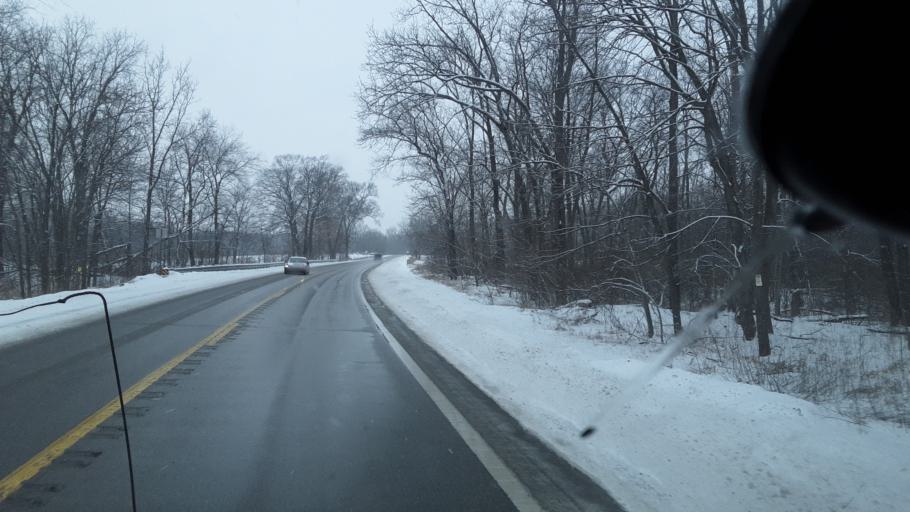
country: US
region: Michigan
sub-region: Jackson County
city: Jackson
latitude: 42.3258
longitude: -84.3647
